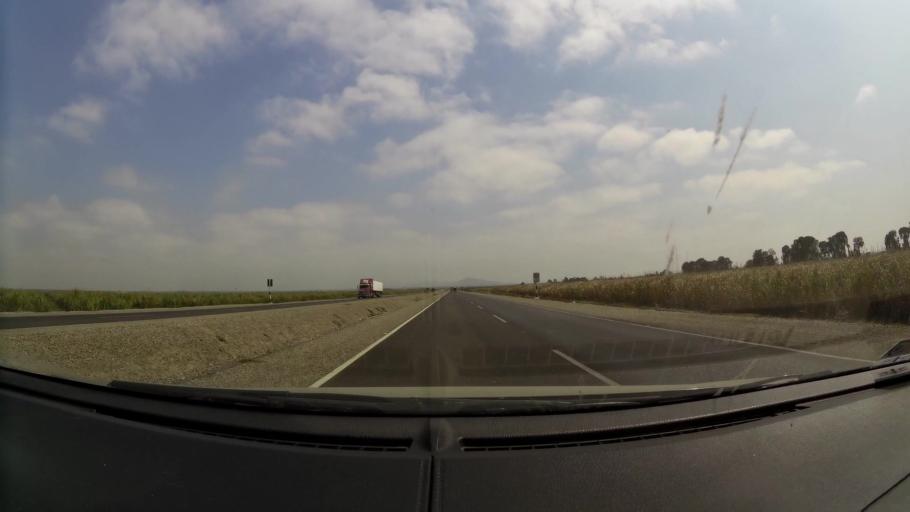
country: PE
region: La Libertad
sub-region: Ascope
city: Chicama
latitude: -7.8593
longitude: -79.1437
